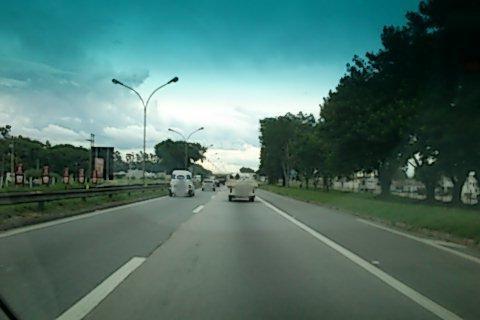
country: BR
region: Sao Paulo
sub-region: Jacarei
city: Jacarei
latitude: -23.2638
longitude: -45.9568
